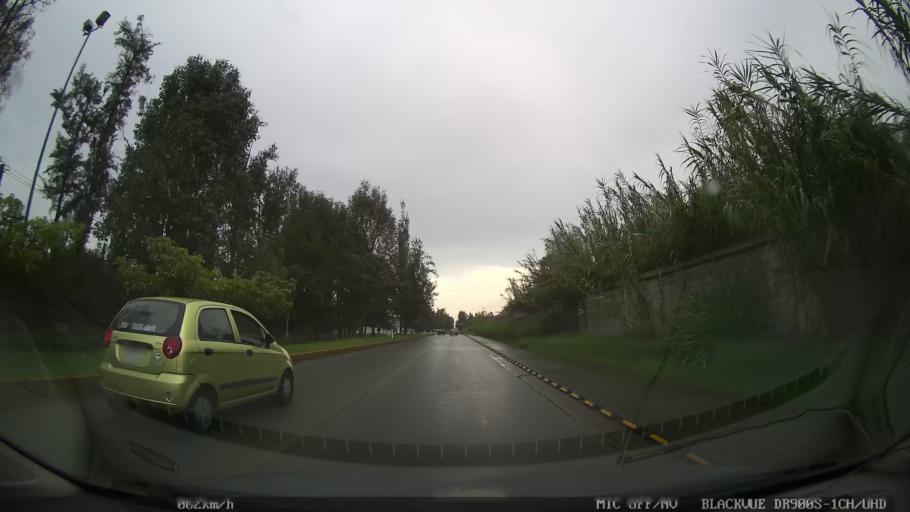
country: MX
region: Michoacan
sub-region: Uruapan
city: Santa Rosa (Santa Barbara)
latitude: 19.4010
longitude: -102.0329
